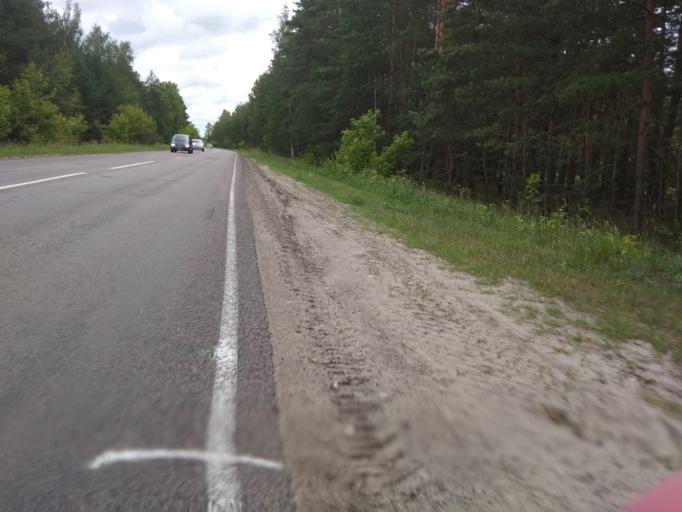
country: RU
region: Moskovskaya
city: Kerva
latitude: 55.5803
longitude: 39.6910
